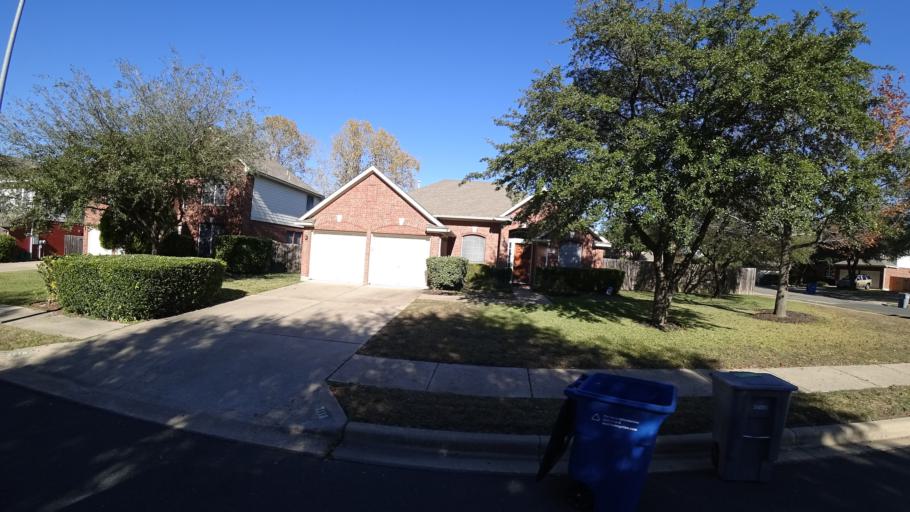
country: US
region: Texas
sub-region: Travis County
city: Wells Branch
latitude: 30.4274
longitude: -97.6906
